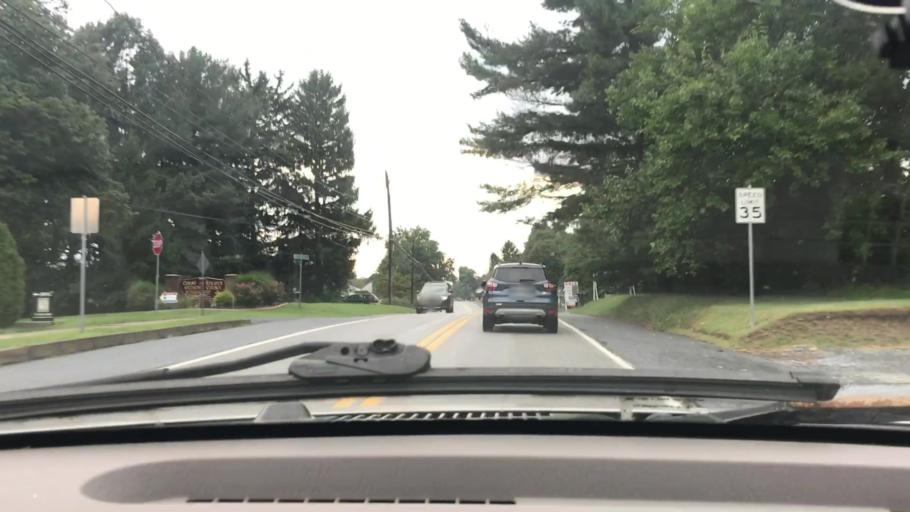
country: US
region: Pennsylvania
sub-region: Dauphin County
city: Colonial Park
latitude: 40.2925
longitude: -76.7939
